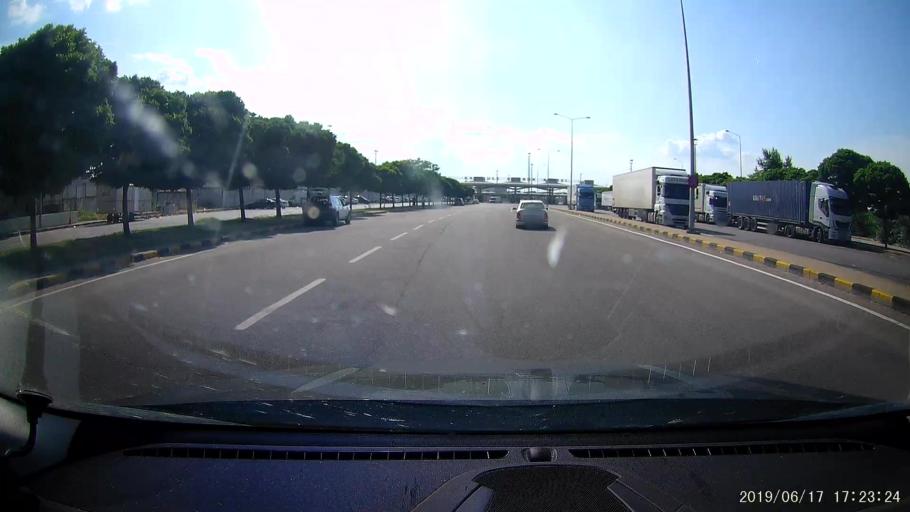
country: GR
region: East Macedonia and Thrace
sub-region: Nomos Evrou
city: Rizia
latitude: 41.7141
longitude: 26.3653
